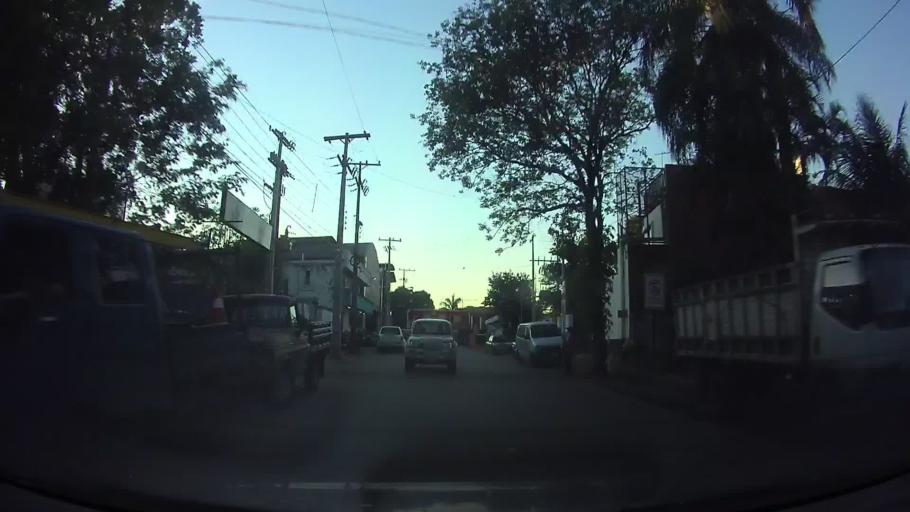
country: PY
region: Central
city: Fernando de la Mora
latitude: -25.3237
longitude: -57.5512
